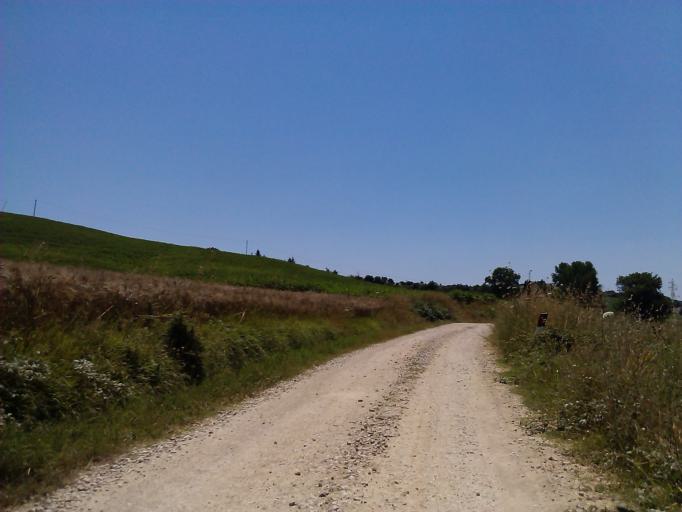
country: IT
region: Umbria
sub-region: Provincia di Terni
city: Fabro Scalo
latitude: 42.8484
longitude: 12.0414
